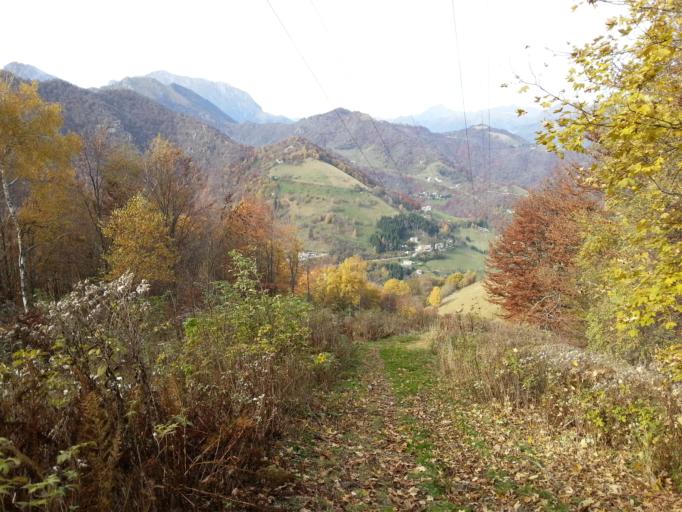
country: IT
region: Lombardy
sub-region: Provincia di Lecco
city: Morterone
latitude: 45.8676
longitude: 9.4885
